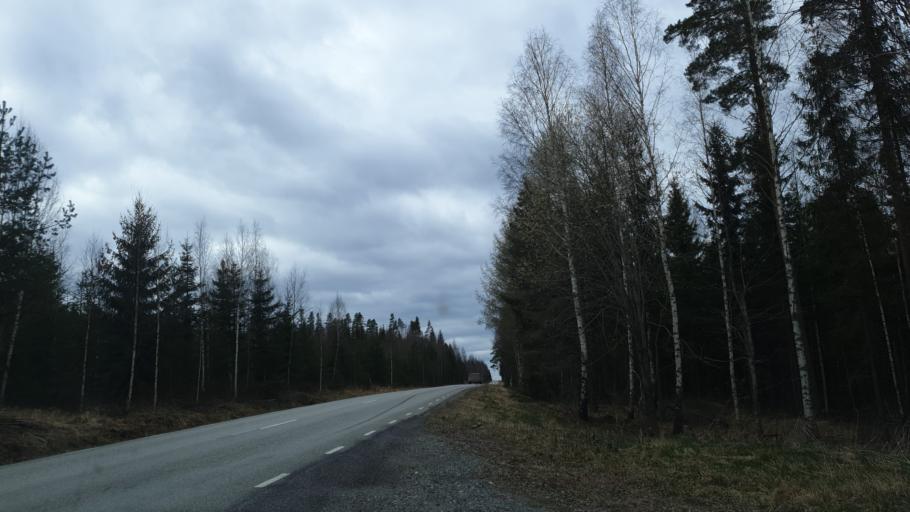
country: SE
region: OErebro
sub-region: Nora Kommun
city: As
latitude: 59.5655
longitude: 15.0036
